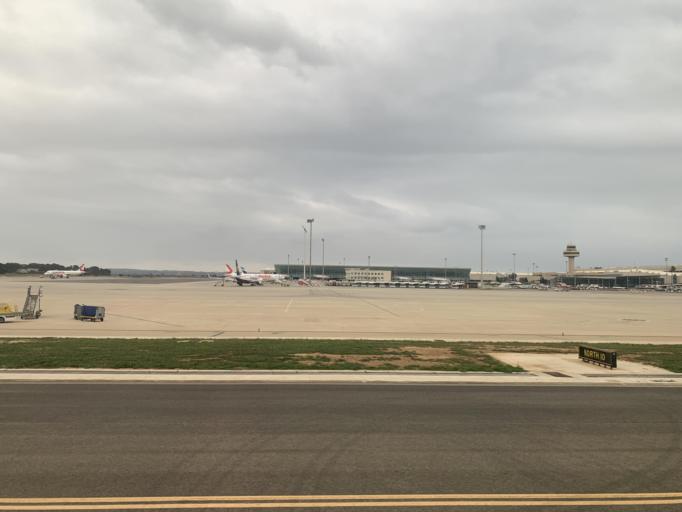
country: ES
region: Balearic Islands
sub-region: Illes Balears
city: s'Arenal
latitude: 39.5557
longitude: 2.7313
